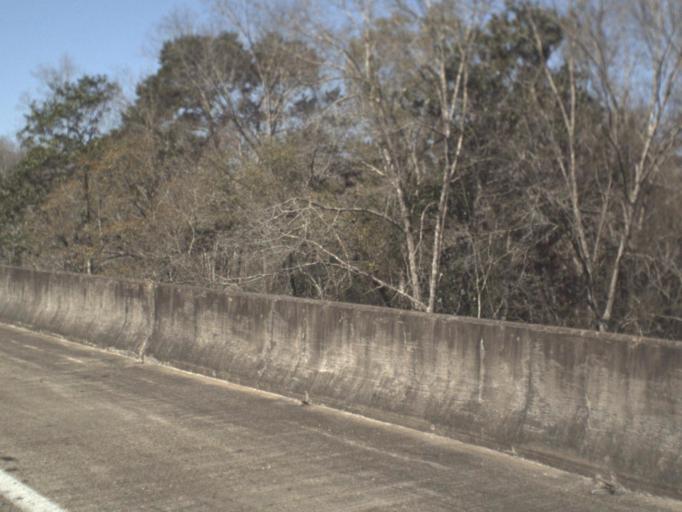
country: US
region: Florida
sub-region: Gadsden County
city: Chattahoochee
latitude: 30.6207
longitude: -84.8093
